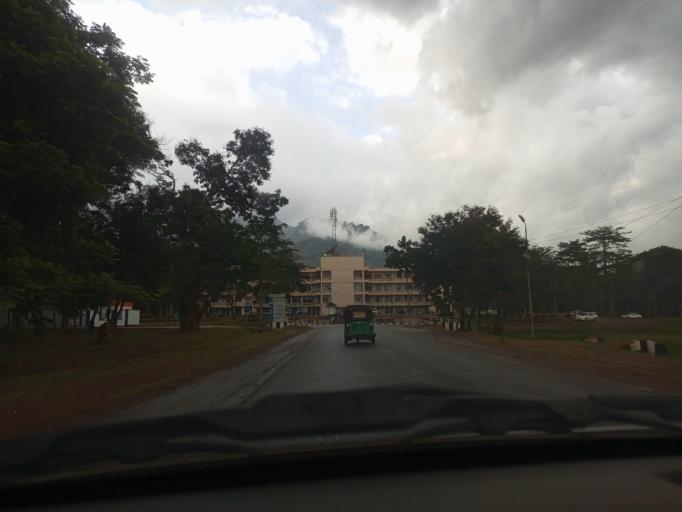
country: TZ
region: Morogoro
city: Morogoro
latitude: -6.8509
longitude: 37.6577
